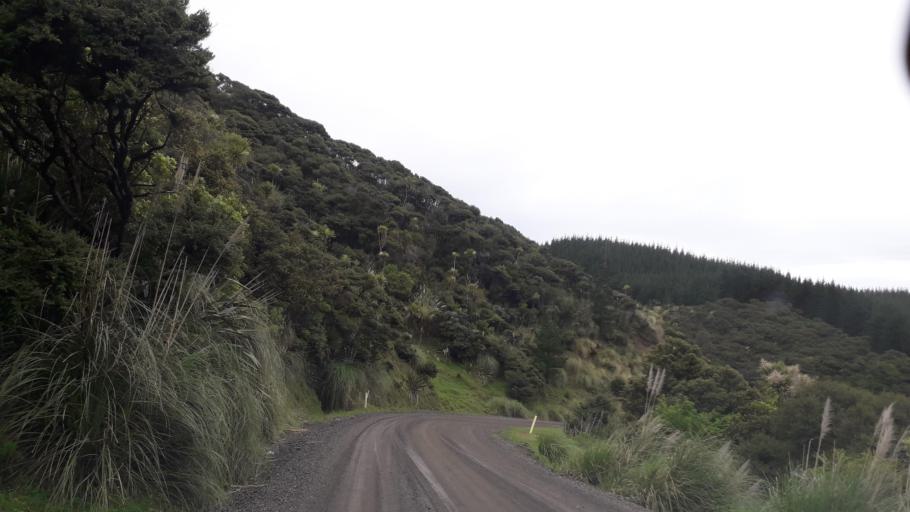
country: NZ
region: Northland
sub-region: Far North District
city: Ahipara
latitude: -35.4396
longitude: 173.3040
